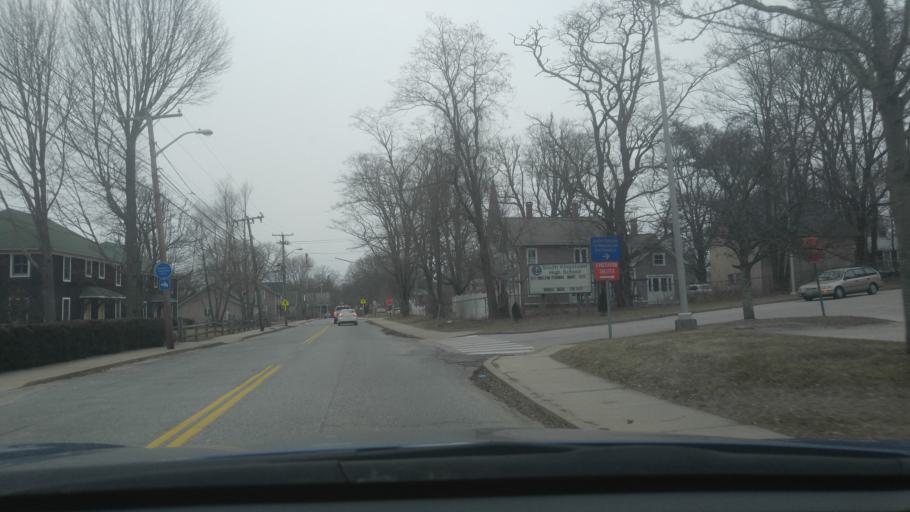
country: US
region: Rhode Island
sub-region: Washington County
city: Wakefield-Peacedale
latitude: 41.4468
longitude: -71.4961
